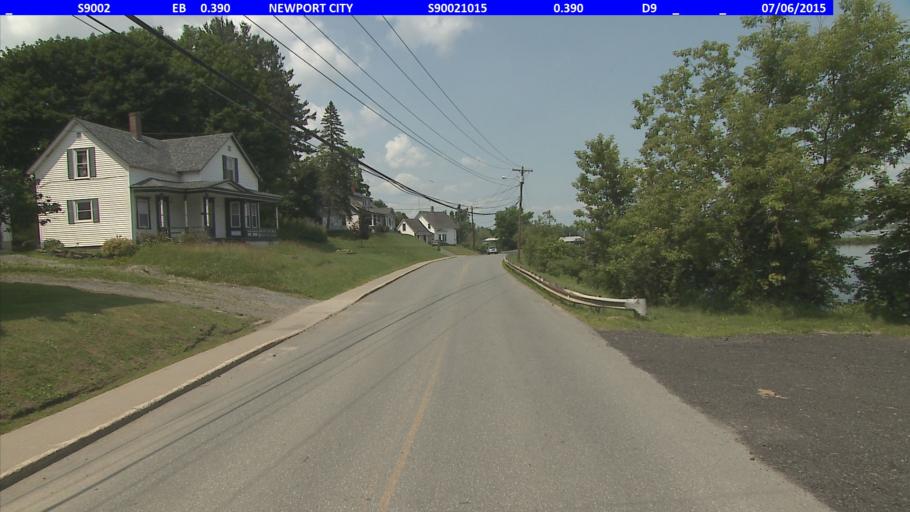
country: US
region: Vermont
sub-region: Orleans County
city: Newport
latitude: 44.9340
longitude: -72.2171
